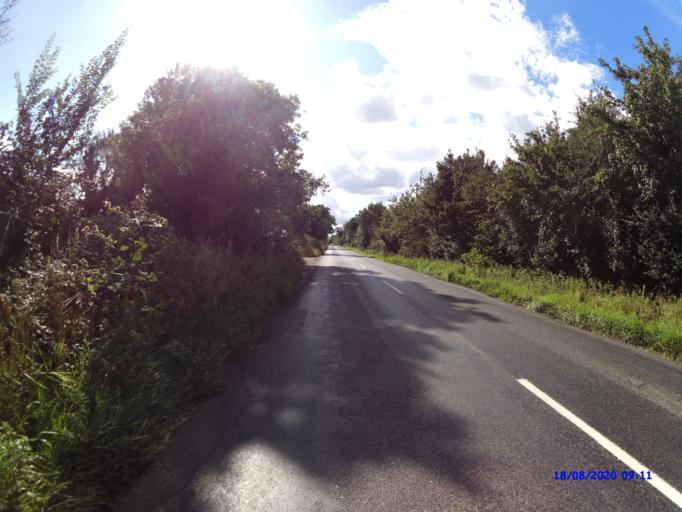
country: GB
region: England
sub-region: Cambridgeshire
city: Ramsey
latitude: 52.4647
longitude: -0.0964
